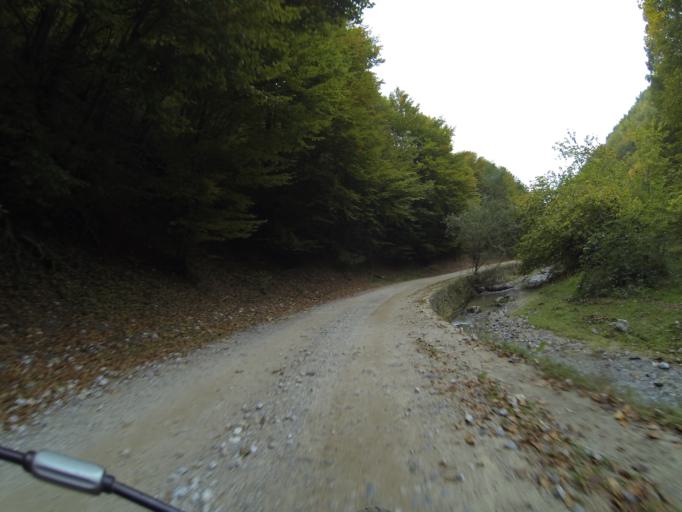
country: RO
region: Gorj
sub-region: Comuna Tismana
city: Sohodol
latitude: 45.0681
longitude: 22.8908
